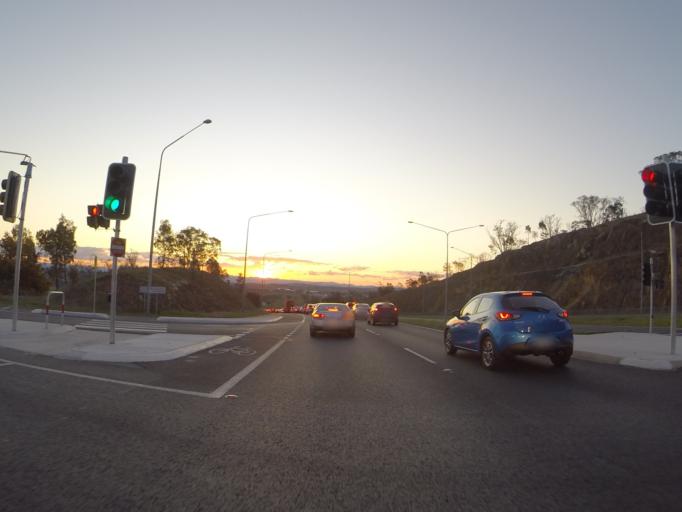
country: AU
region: Australian Capital Territory
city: Kaleen
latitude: -35.2133
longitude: 149.1849
